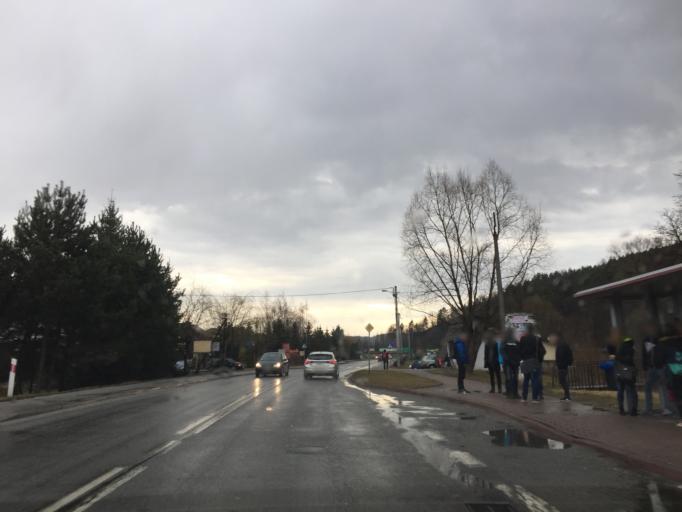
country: PL
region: Lesser Poland Voivodeship
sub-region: Powiat myslenicki
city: Sulkowice
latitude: 49.8544
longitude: 19.7994
